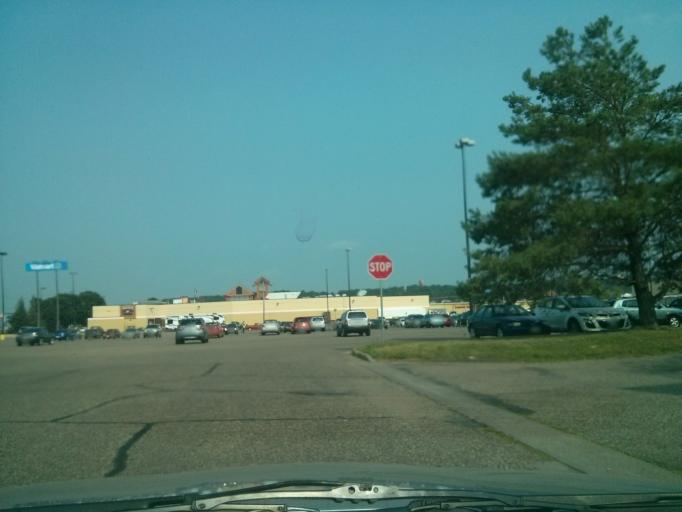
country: US
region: Wisconsin
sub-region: Saint Croix County
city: Hudson
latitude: 44.9602
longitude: -92.7282
